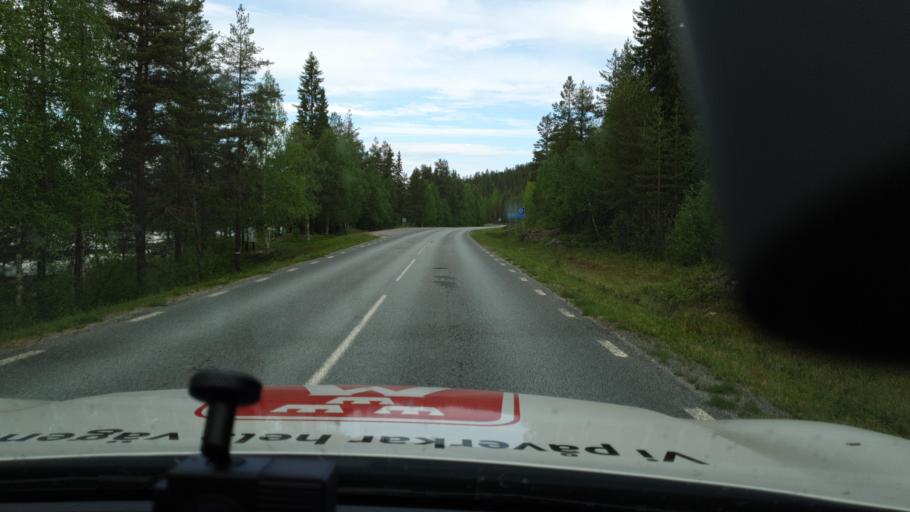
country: SE
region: Vaesterbotten
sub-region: Lycksele Kommun
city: Soderfors
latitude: 65.0757
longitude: 18.3436
